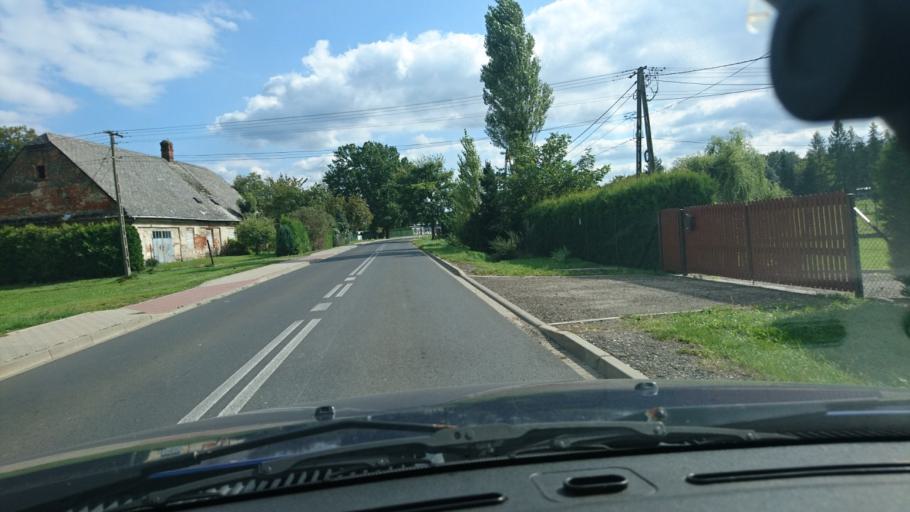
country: PL
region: Silesian Voivodeship
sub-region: Powiat bielski
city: Mazancowice
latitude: 49.8599
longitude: 18.9755
